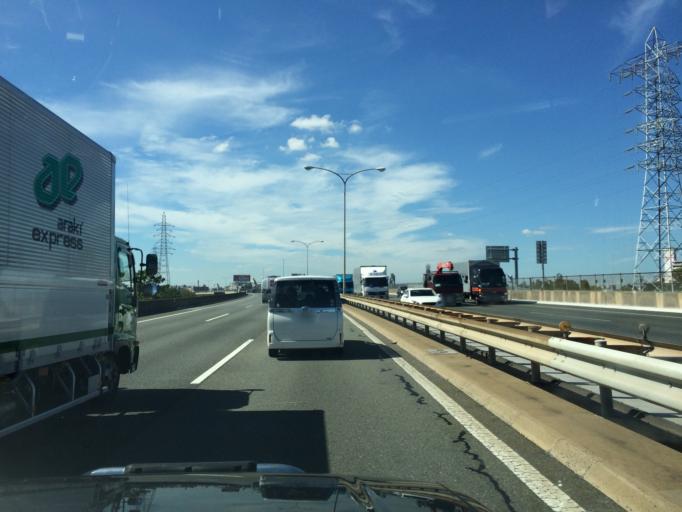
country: JP
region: Osaka
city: Yao
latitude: 34.6297
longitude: 135.5813
